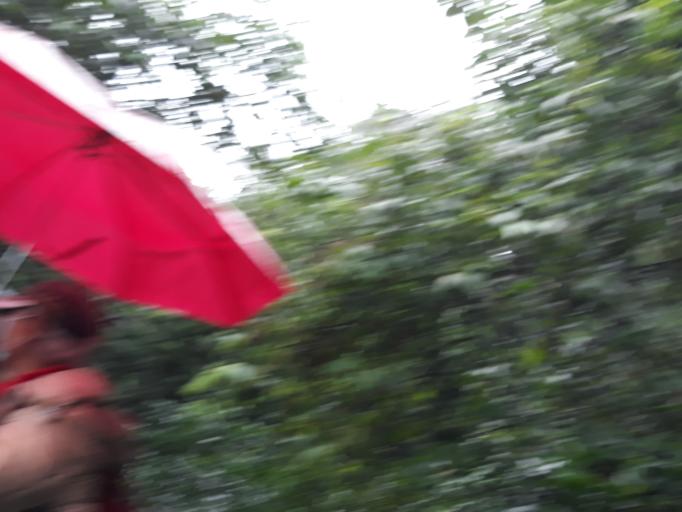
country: TW
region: Taipei
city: Taipei
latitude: 24.9957
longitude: 121.5900
